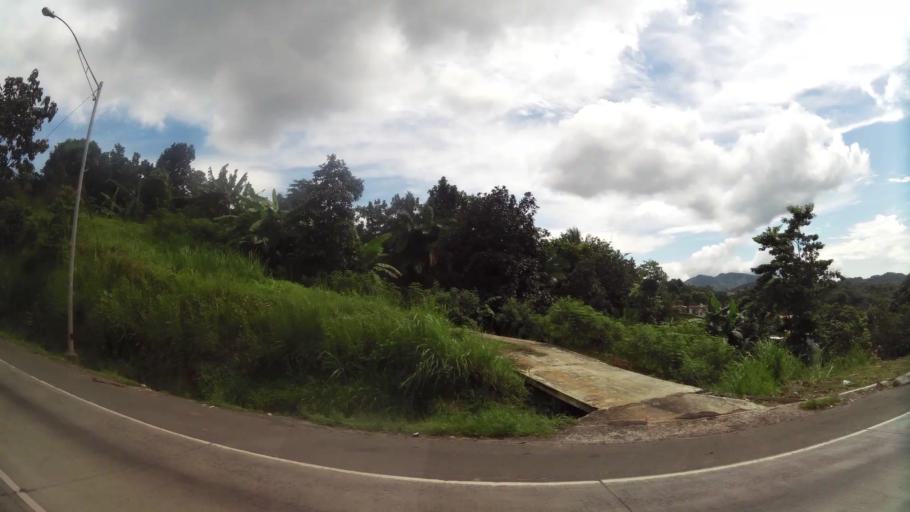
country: PA
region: Panama
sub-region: Distrito Arraijan
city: Arraijan
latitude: 8.9595
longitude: -79.6594
